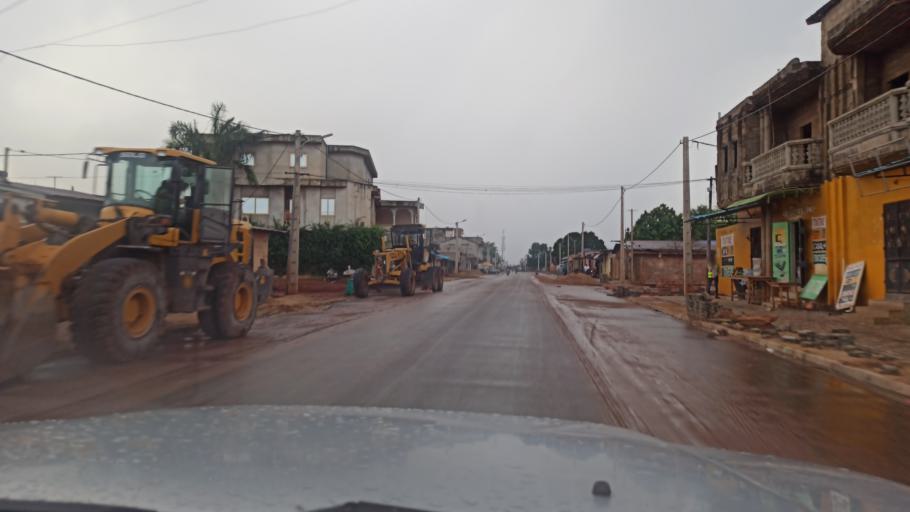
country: BJ
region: Queme
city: Porto-Novo
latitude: 6.4941
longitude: 2.6450
